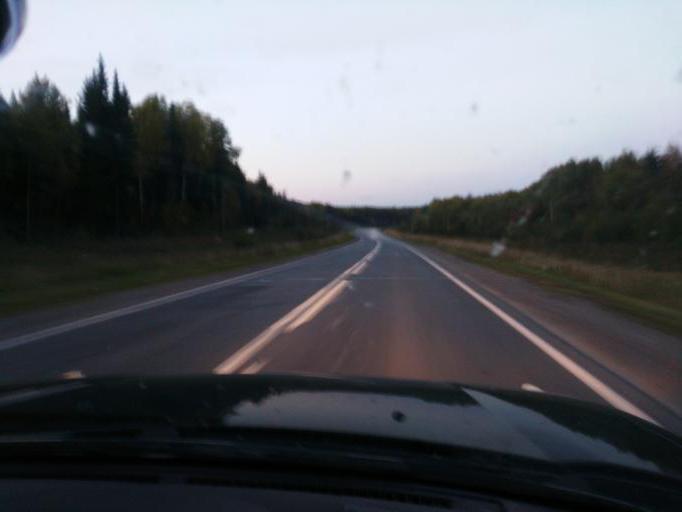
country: RU
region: Perm
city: Verkhnechusovskiye Gorodki
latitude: 58.2339
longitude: 57.2152
